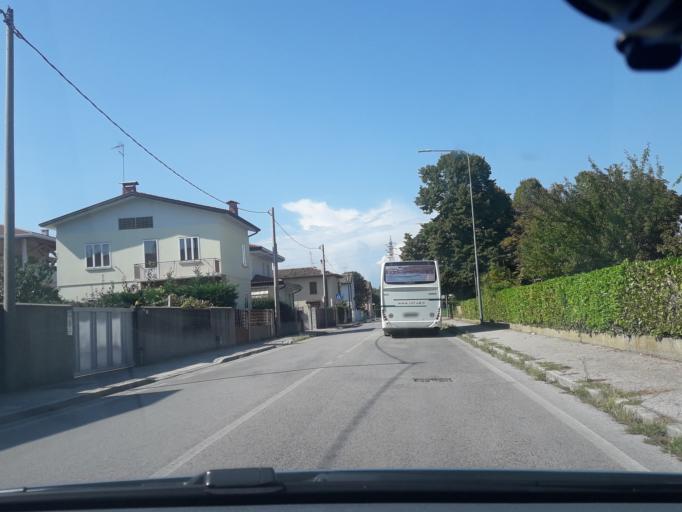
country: IT
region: Friuli Venezia Giulia
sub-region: Provincia di Udine
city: Colugna
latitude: 46.0756
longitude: 13.2069
